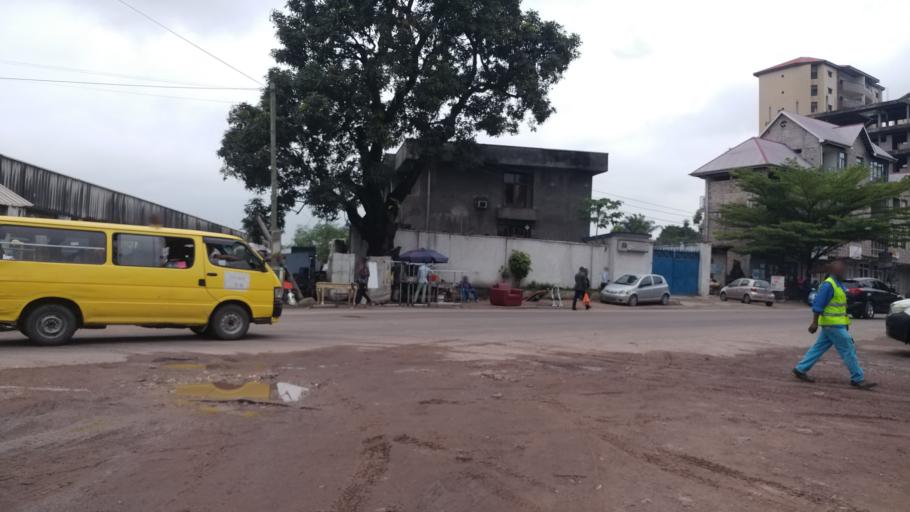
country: CD
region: Kinshasa
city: Kinshasa
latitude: -4.3218
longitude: 15.2760
